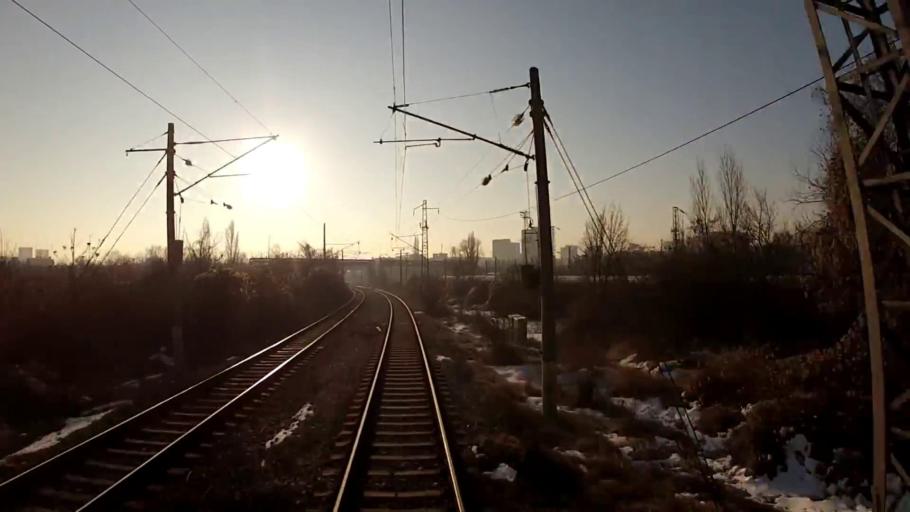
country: BG
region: Sofia-Capital
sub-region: Stolichna Obshtina
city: Sofia
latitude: 42.7253
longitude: 23.2888
